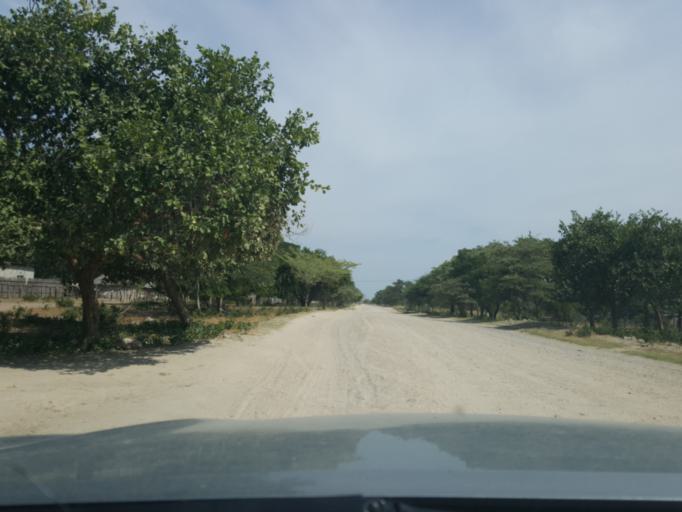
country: BW
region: North West
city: Shakawe
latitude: -18.3119
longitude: 21.8963
